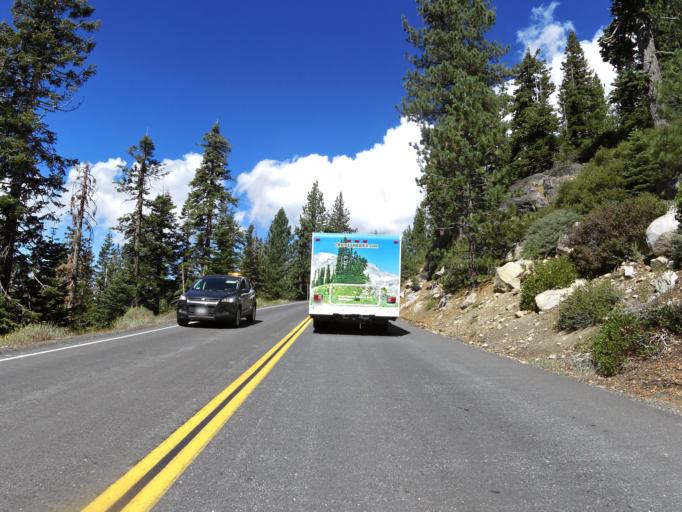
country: US
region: California
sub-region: El Dorado County
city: South Lake Tahoe
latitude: 38.6858
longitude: -120.1221
